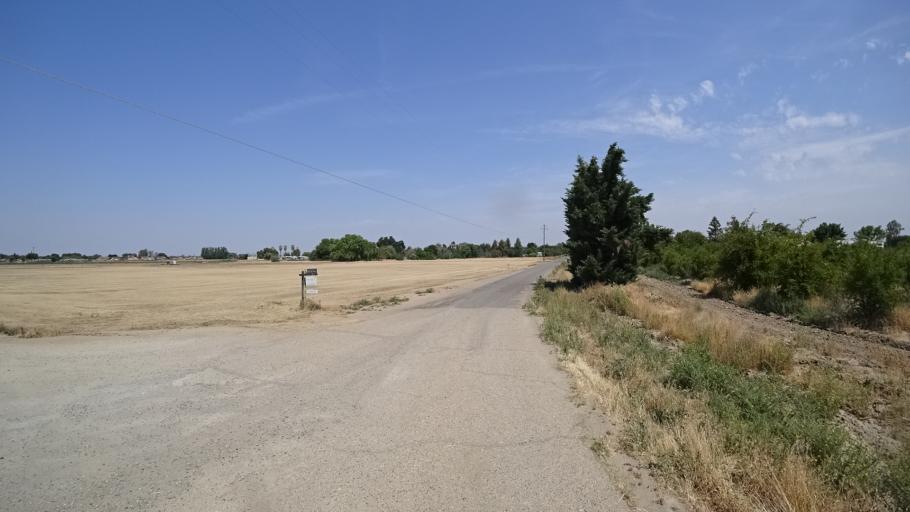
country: US
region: California
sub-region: Kings County
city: Lemoore
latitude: 36.2948
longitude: -119.7628
